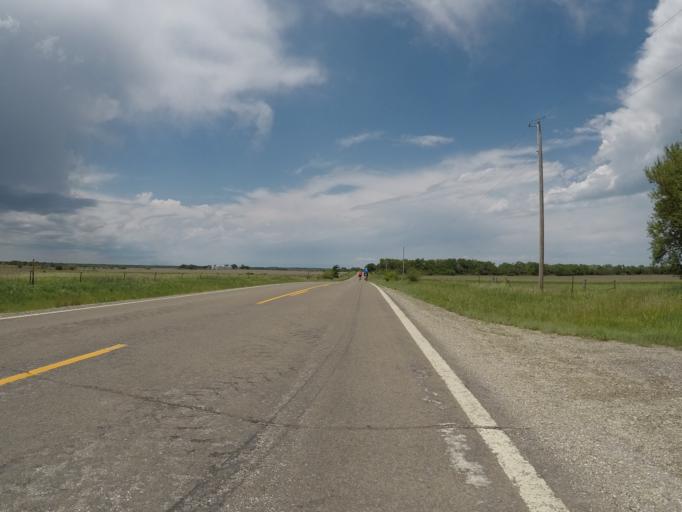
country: US
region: Kansas
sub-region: Morris County
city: Council Grove
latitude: 38.8545
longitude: -96.4334
